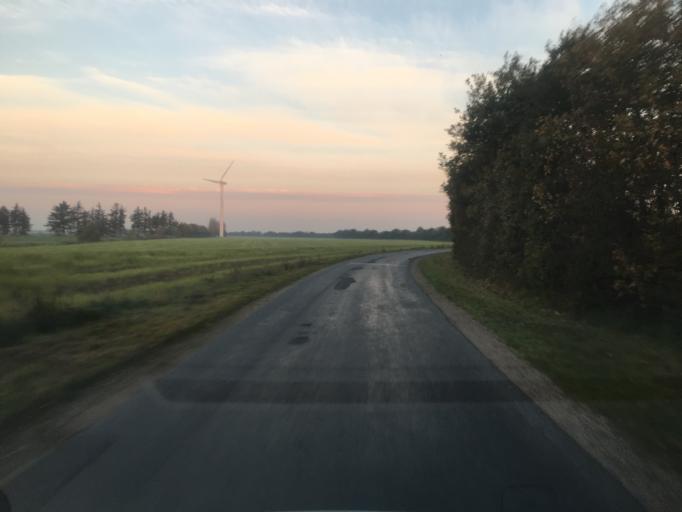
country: DK
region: South Denmark
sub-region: Tonder Kommune
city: Logumkloster
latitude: 54.9867
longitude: 9.0536
